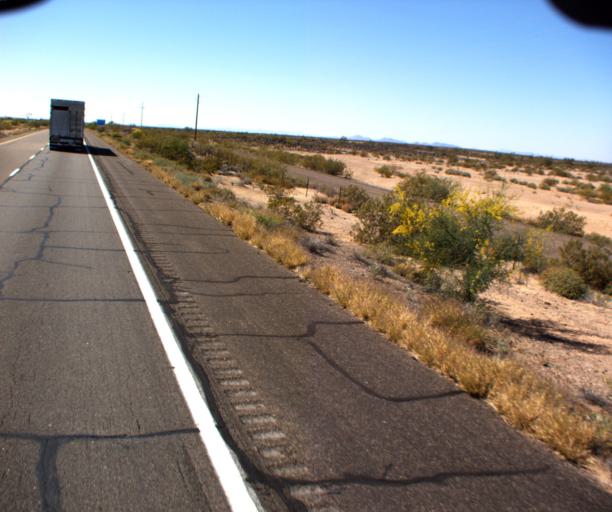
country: US
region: Arizona
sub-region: Maricopa County
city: Gila Bend
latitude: 32.8565
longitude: -113.2380
